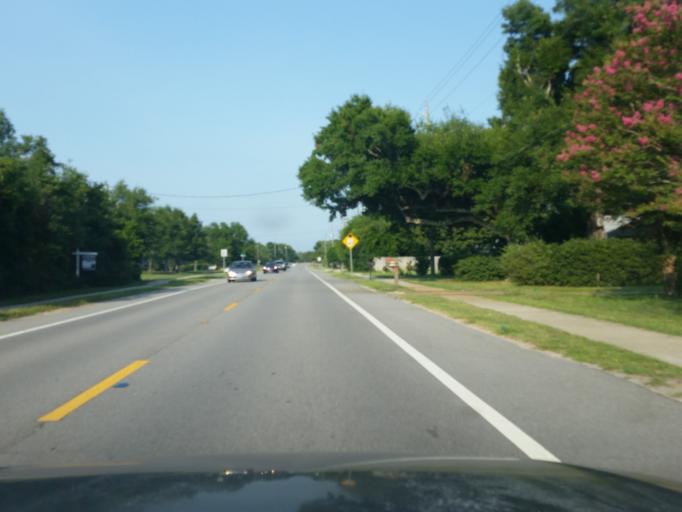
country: US
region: Florida
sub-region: Escambia County
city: Myrtle Grove
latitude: 30.3255
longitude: -87.3840
